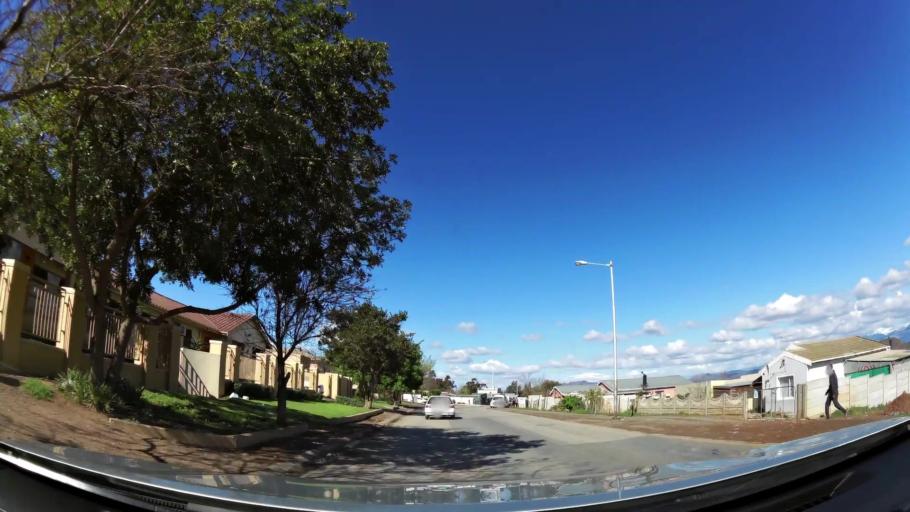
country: ZA
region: Western Cape
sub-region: Cape Winelands District Municipality
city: Ashton
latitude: -33.7910
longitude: 19.8930
